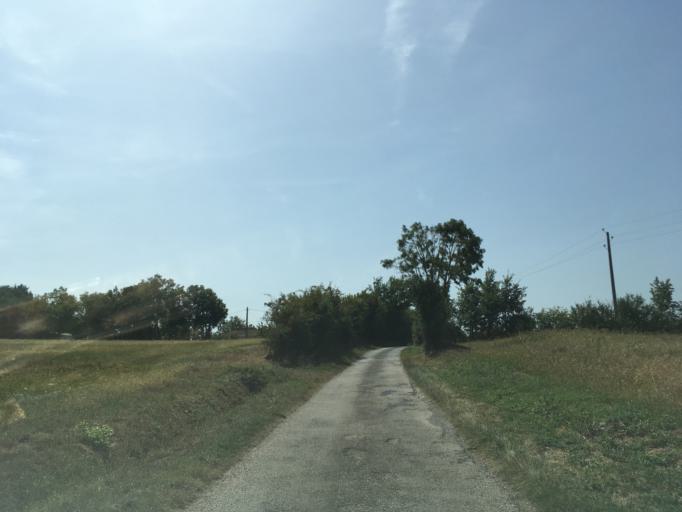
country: FR
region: Midi-Pyrenees
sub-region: Departement du Tarn
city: Lagarrigue
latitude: 43.6121
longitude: 2.2859
